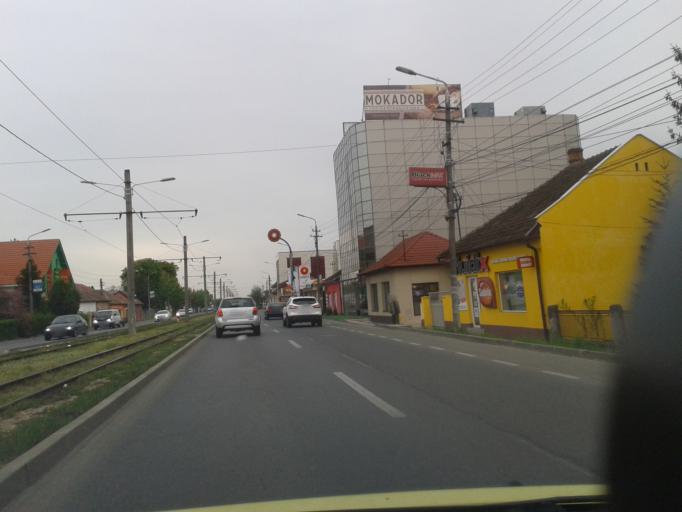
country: RO
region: Arad
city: Arad
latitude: 46.1789
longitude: 21.3497
